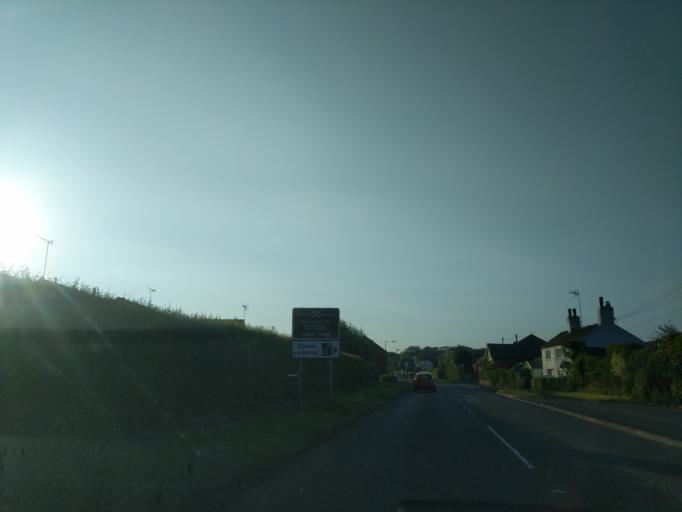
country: GB
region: England
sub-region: Staffordshire
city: Stone
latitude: 52.8892
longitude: -2.1245
